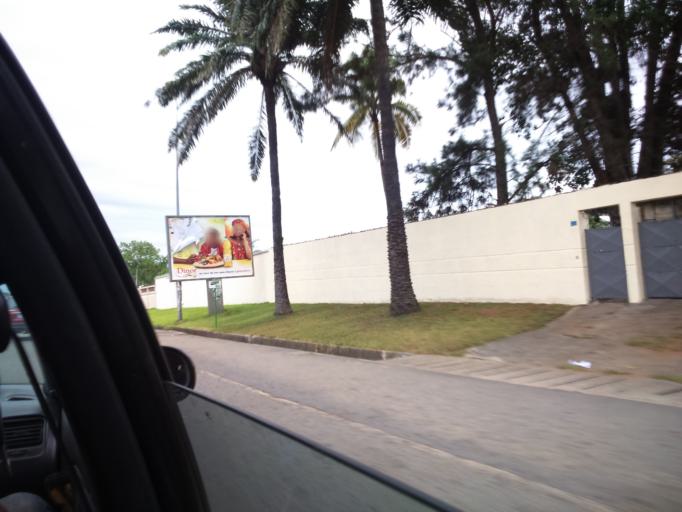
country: CI
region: Lagunes
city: Abidjan
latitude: 5.3516
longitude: -3.9913
